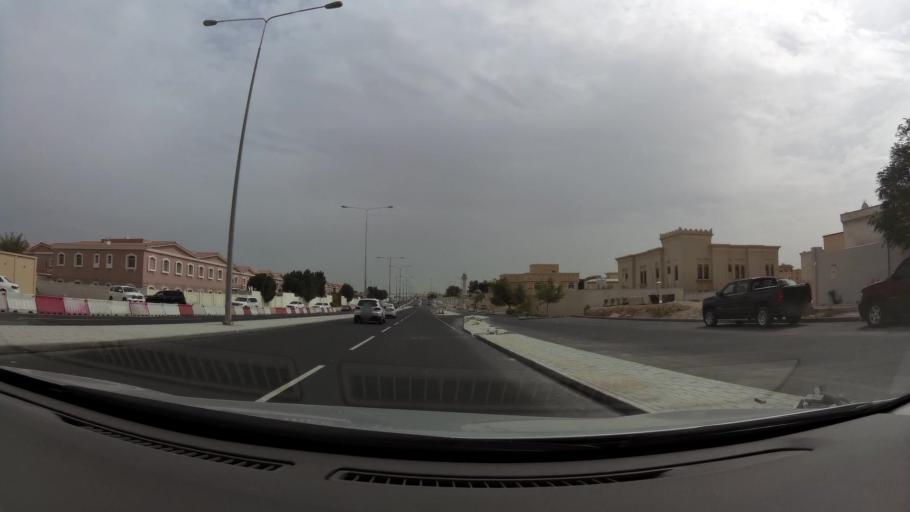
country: QA
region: Baladiyat ar Rayyan
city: Ar Rayyan
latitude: 25.3524
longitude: 51.4655
